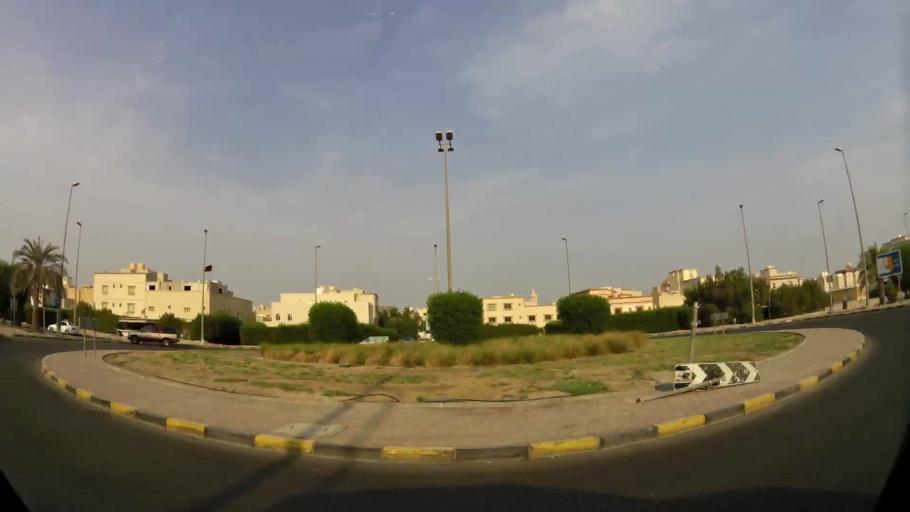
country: KW
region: Mubarak al Kabir
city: Mubarak al Kabir
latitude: 29.2166
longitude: 48.0628
